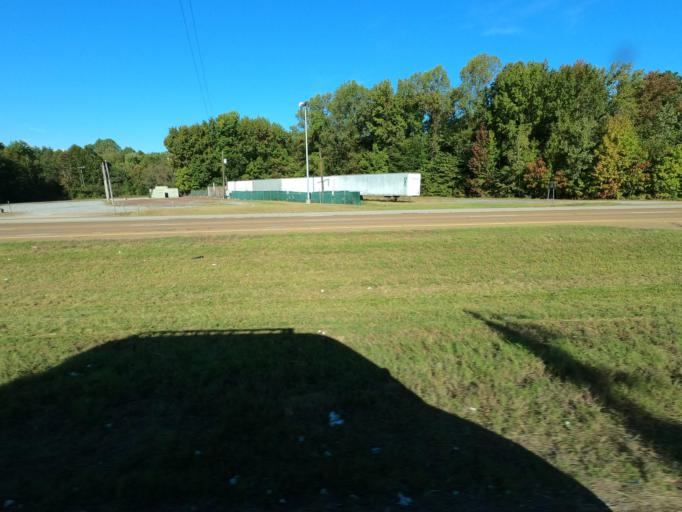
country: US
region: Tennessee
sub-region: Shelby County
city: Millington
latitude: 35.3930
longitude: -89.8535
